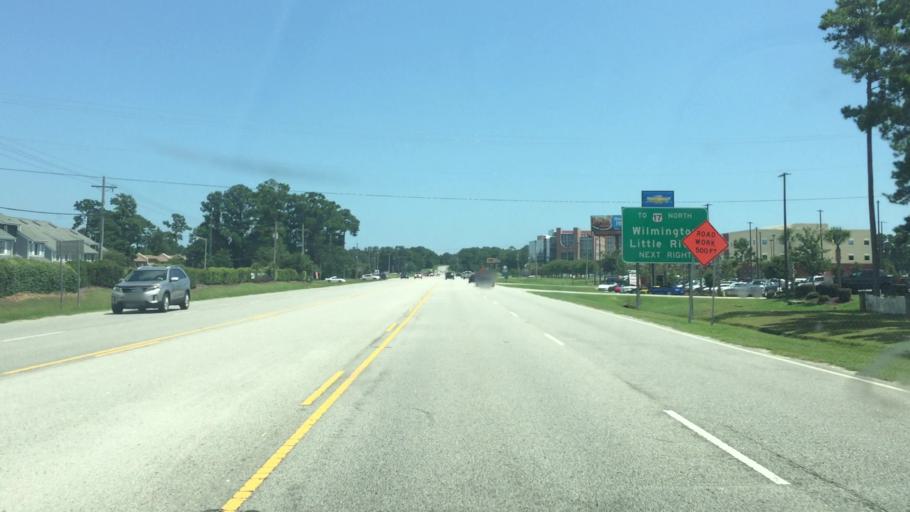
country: US
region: South Carolina
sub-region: Horry County
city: Little River
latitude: 33.8688
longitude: -78.6674
